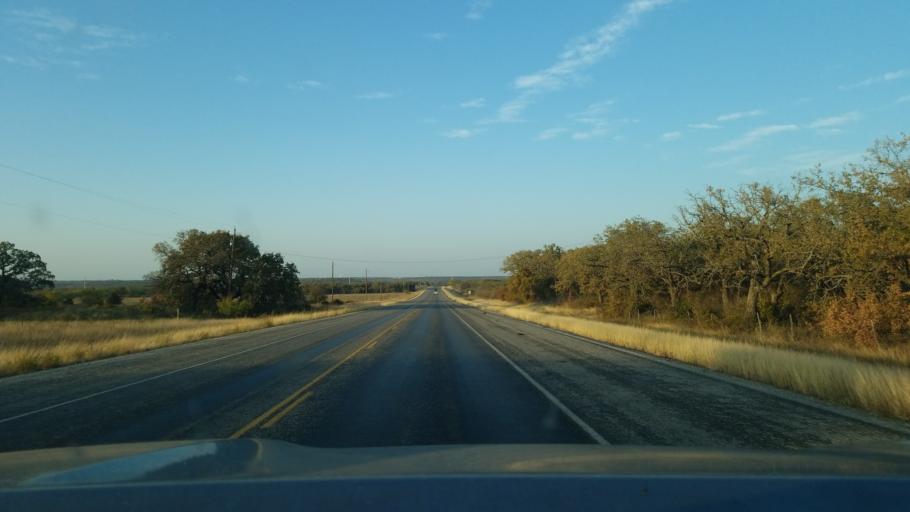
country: US
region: Texas
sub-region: Eastland County
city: Cisco
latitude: 32.3243
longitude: -98.9575
